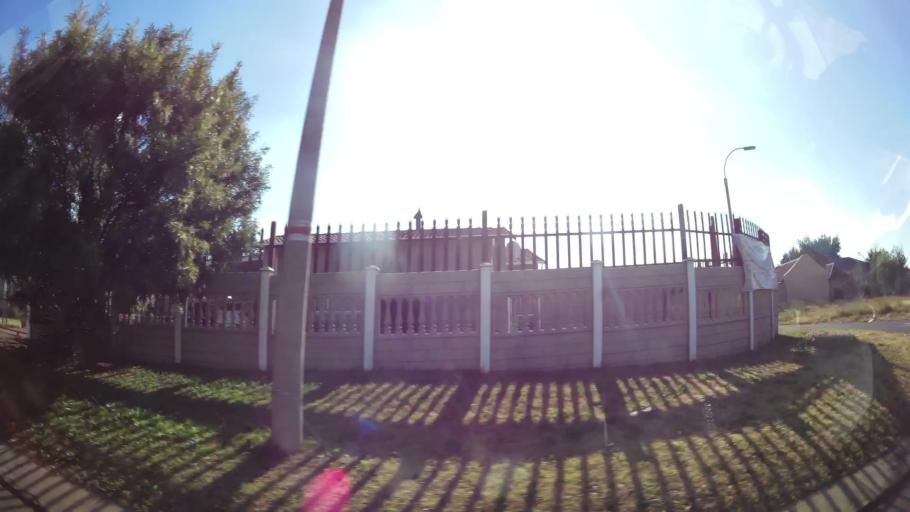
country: ZA
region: Gauteng
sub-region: City of Johannesburg Metropolitan Municipality
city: Roodepoort
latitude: -26.1655
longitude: 27.8220
